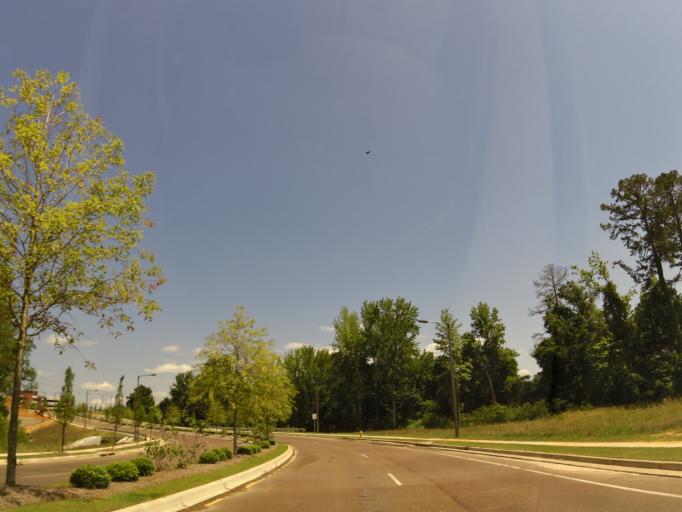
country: US
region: Mississippi
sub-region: Lafayette County
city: University
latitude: 34.3477
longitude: -89.5246
